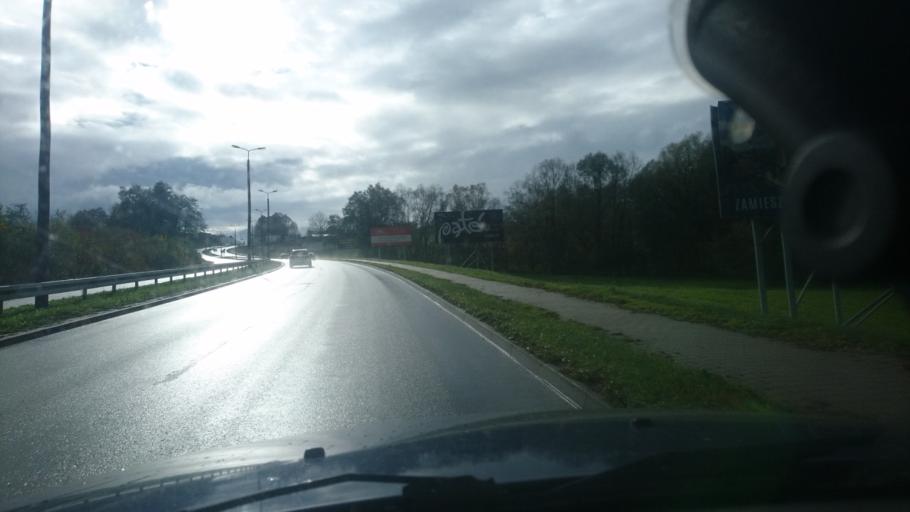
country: PL
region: Silesian Voivodeship
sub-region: Bielsko-Biala
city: Bielsko-Biala
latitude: 49.8336
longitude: 19.0094
